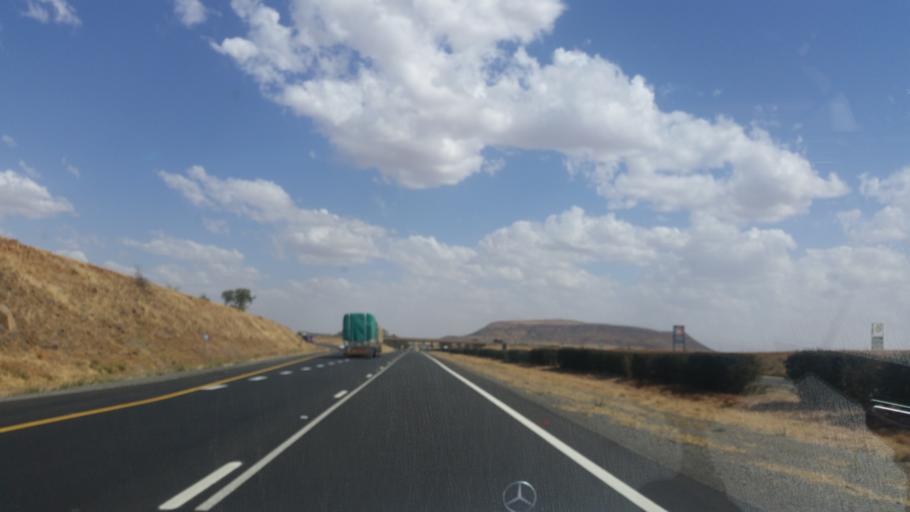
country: ZA
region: Orange Free State
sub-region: Mangaung Metropolitan Municipality
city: Bloemfontein
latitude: -29.1972
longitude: 26.1922
